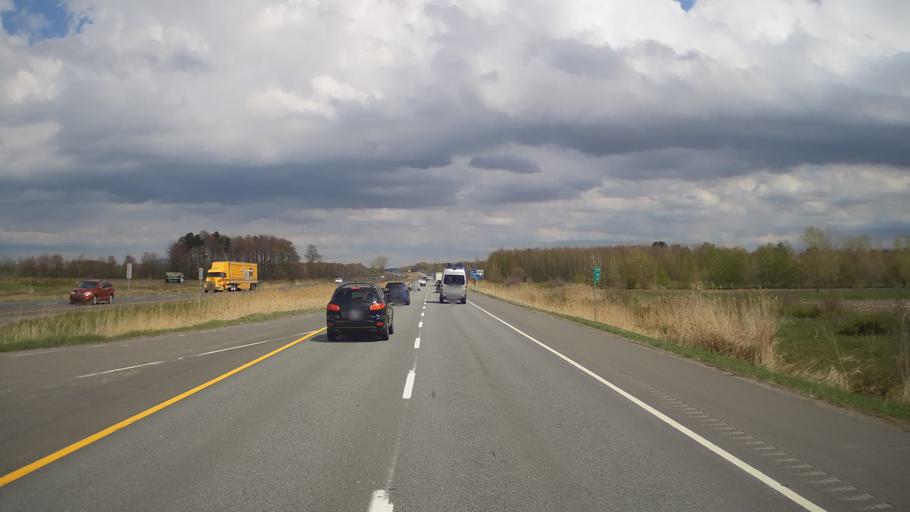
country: CA
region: Quebec
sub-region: Monteregie
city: Granby
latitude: 45.3506
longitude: -72.8523
